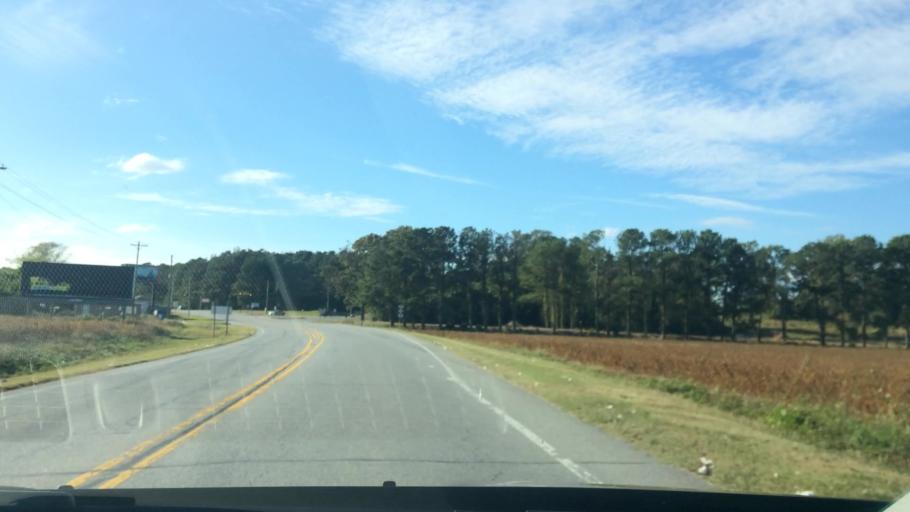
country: US
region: North Carolina
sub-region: Greene County
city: Snow Hill
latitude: 35.4592
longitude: -77.7015
